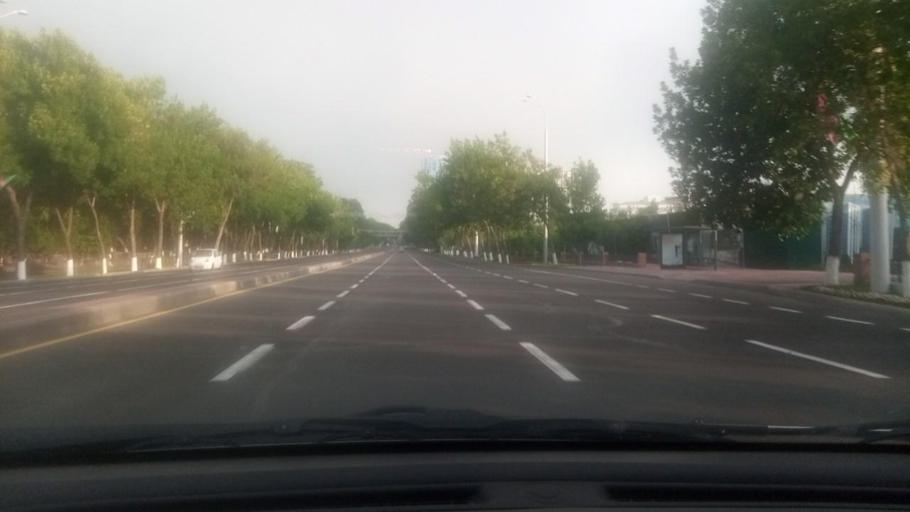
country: UZ
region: Toshkent
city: Salor
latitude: 41.3355
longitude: 69.3445
